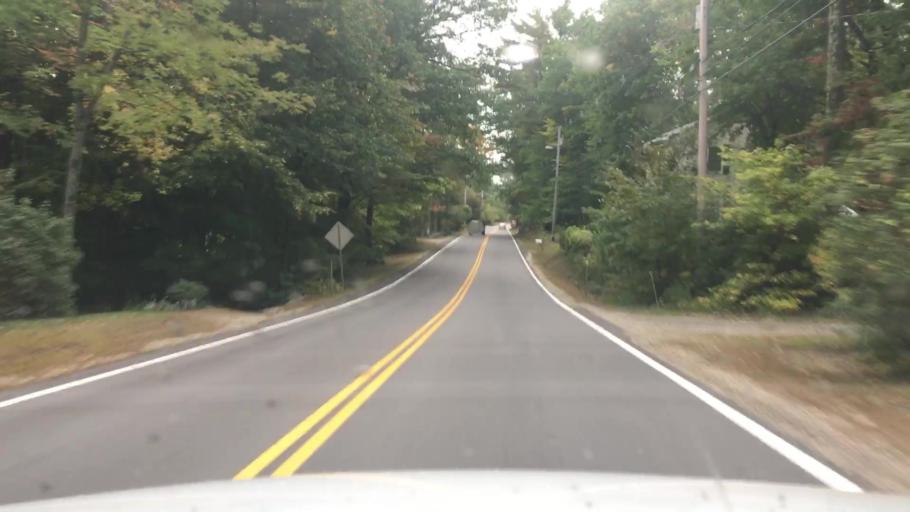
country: US
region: New Hampshire
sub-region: Belknap County
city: Gilford
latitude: 43.5511
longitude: -71.3108
